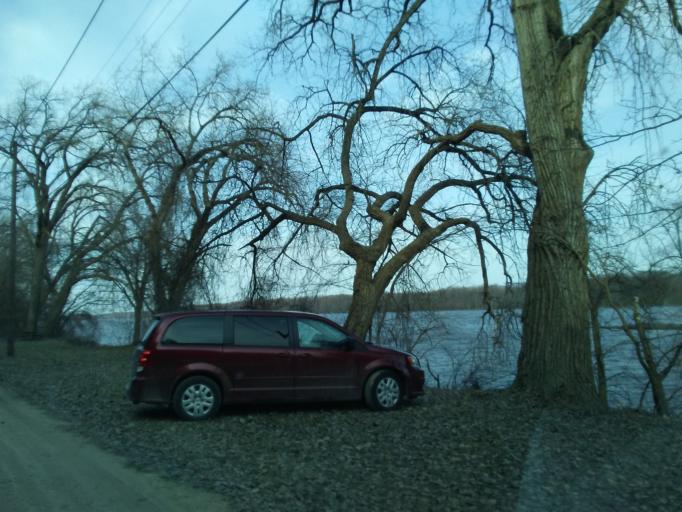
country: US
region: Wisconsin
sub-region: Crawford County
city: Prairie du Chien
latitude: 43.0677
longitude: -91.1802
